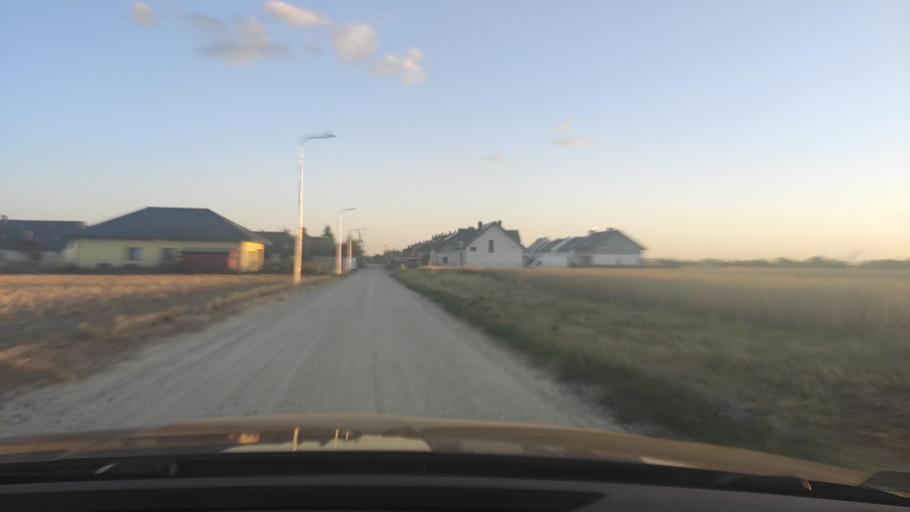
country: PL
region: Greater Poland Voivodeship
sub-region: Powiat poznanski
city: Swarzedz
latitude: 52.4320
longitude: 17.1150
